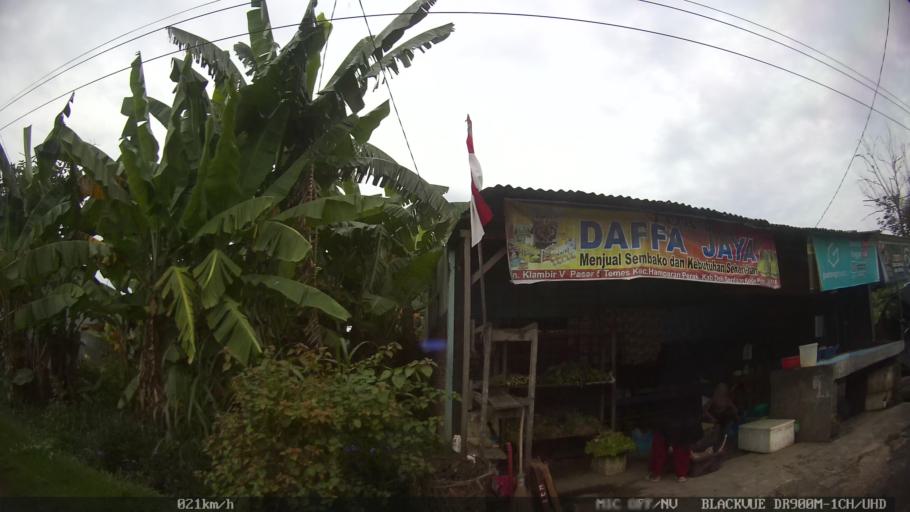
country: ID
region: North Sumatra
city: Sunggal
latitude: 3.6556
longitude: 98.5937
